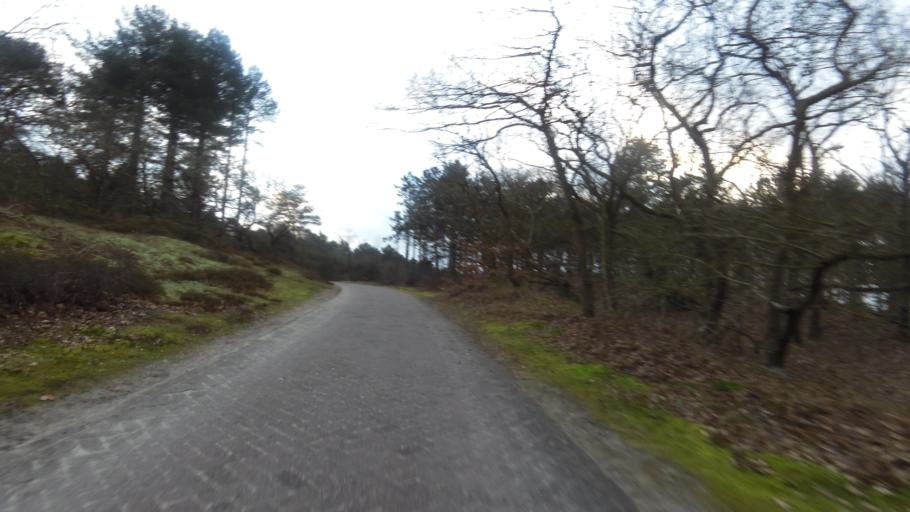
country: NL
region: North Holland
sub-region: Gemeente Heiloo
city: Heiloo
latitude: 52.6792
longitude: 4.6868
